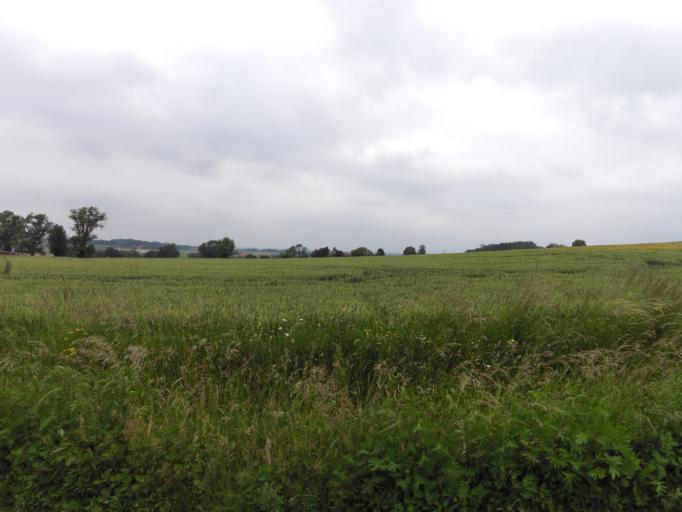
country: FR
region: Nord-Pas-de-Calais
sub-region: Departement du Nord
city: Bailleul
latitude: 50.7800
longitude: 2.8034
